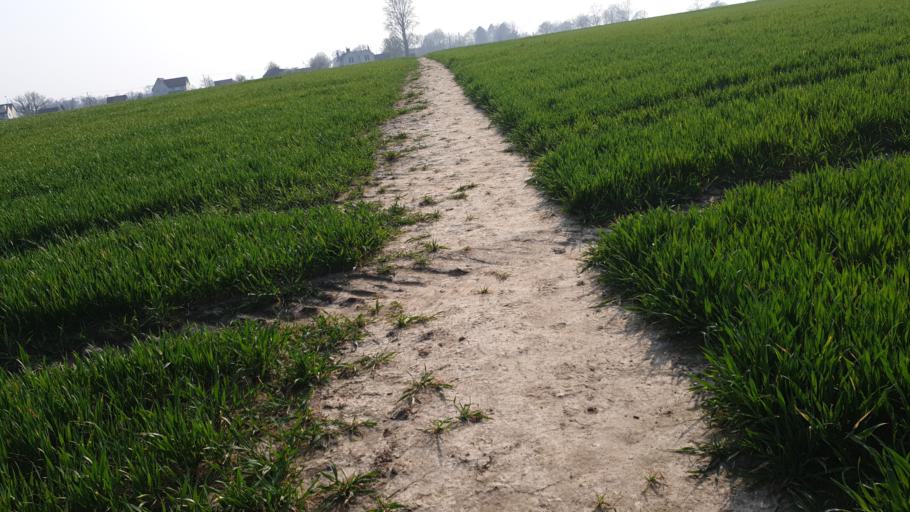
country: GB
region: England
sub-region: Essex
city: Great Bentley
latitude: 51.8841
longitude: 1.1187
